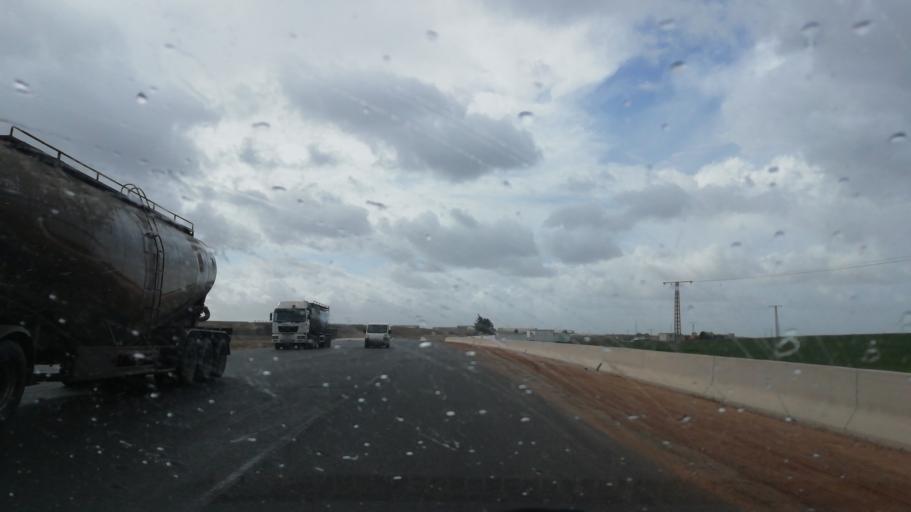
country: DZ
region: Oran
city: Sidi ech Chahmi
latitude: 35.6455
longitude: -0.5249
